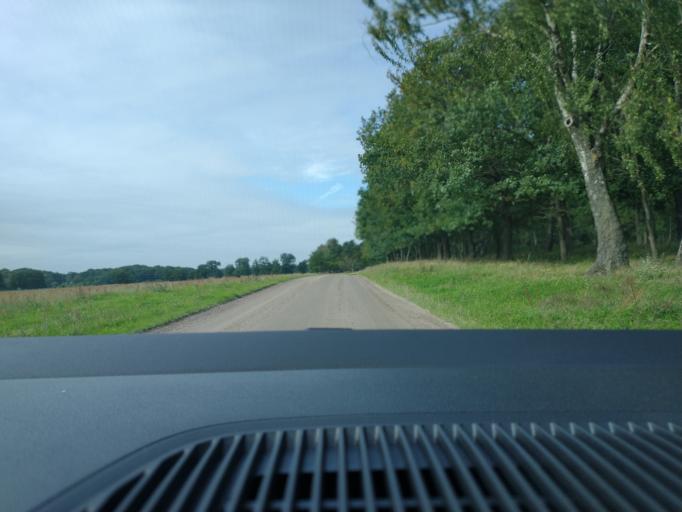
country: SE
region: Skane
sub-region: Lunds Kommun
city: Veberod
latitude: 55.6669
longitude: 13.4629
